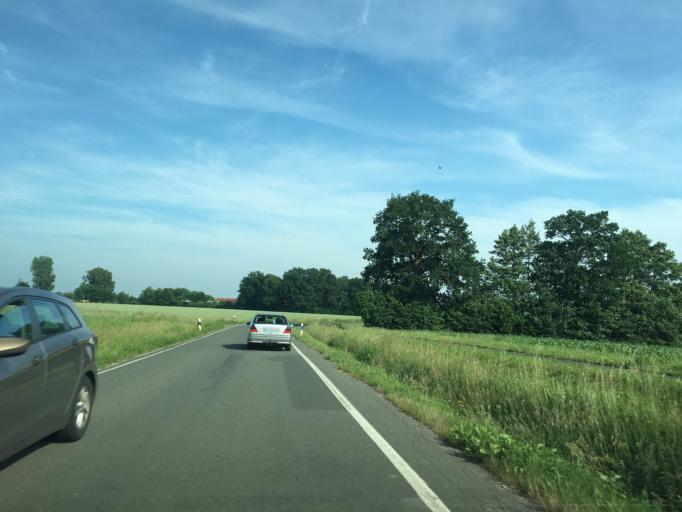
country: DE
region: North Rhine-Westphalia
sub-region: Regierungsbezirk Munster
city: Nordwalde
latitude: 52.1100
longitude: 7.4612
